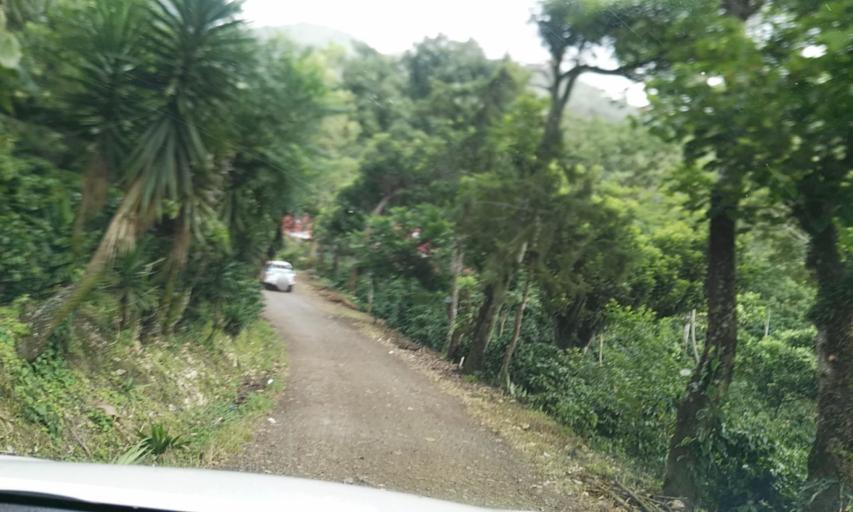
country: NI
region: Matagalpa
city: San Ramon
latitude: 13.0073
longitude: -85.8728
